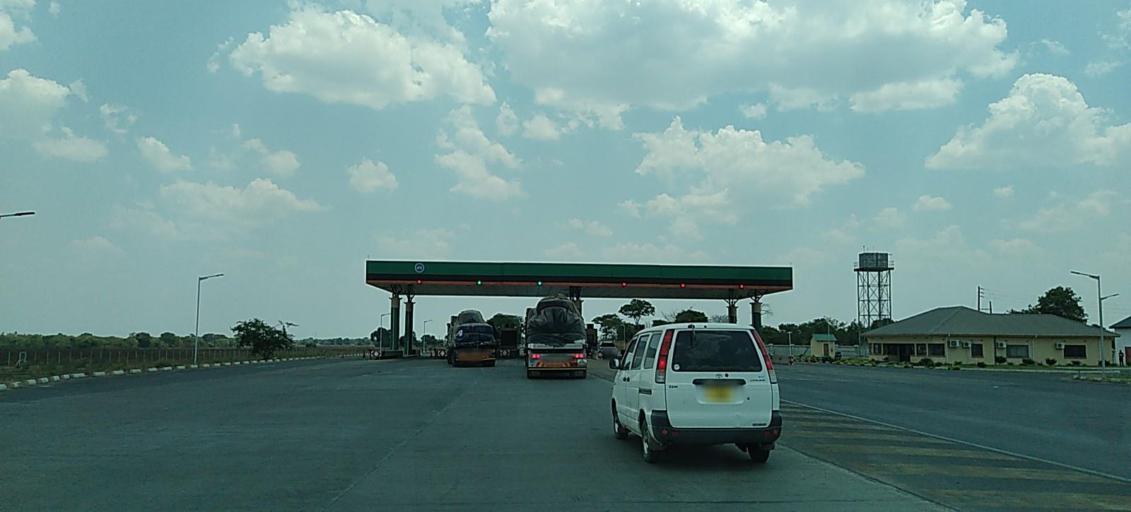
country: ZM
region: Central
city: Kabwe
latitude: -14.2493
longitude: 28.5626
